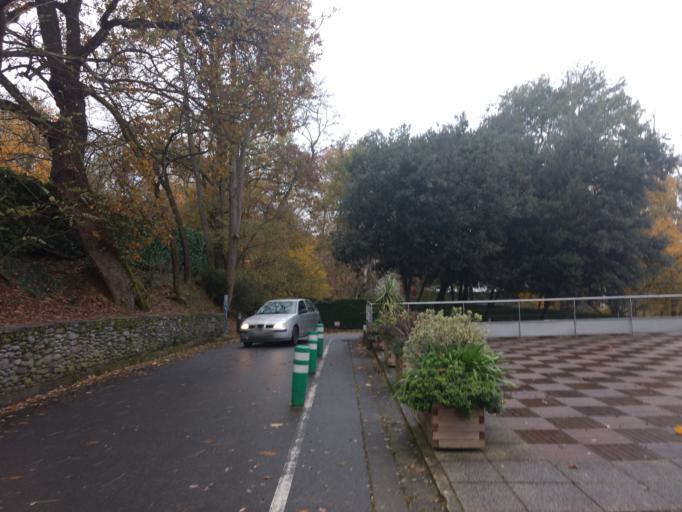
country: FR
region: Midi-Pyrenees
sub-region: Departement de la Haute-Garonne
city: Ramonville-Saint-Agne
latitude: 43.5567
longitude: 1.4616
